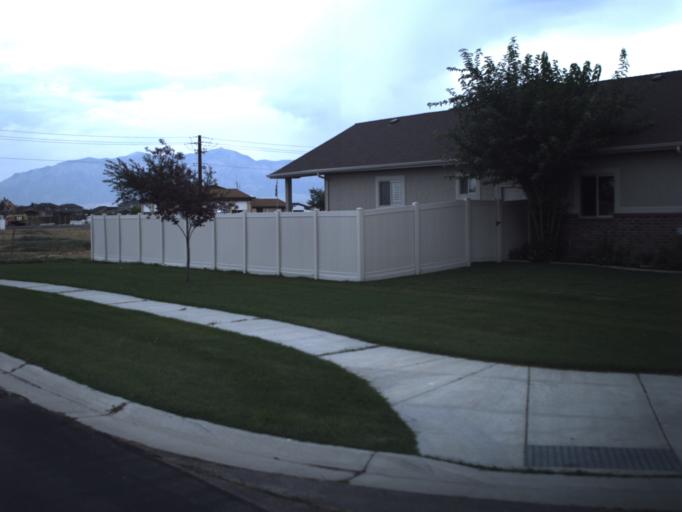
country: US
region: Utah
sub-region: Weber County
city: Hooper
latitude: 41.1896
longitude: -112.0930
